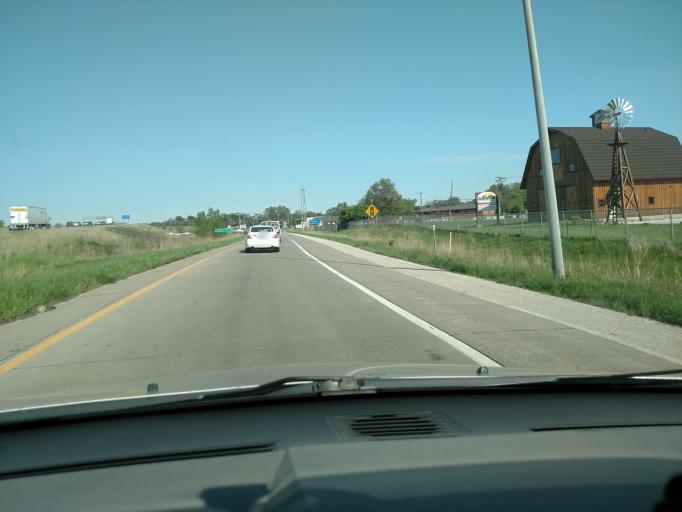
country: US
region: Iowa
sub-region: Polk County
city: Saylorville
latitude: 41.6492
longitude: -93.6238
